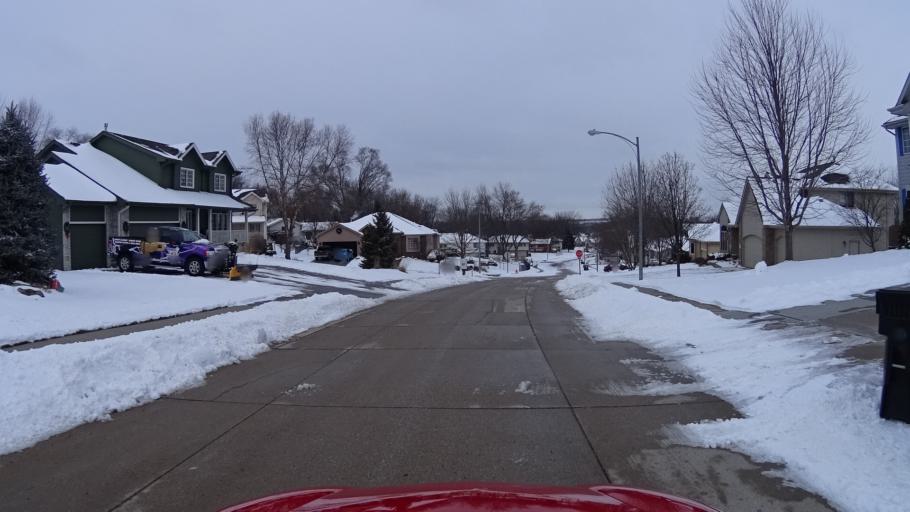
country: US
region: Nebraska
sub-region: Sarpy County
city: Offutt Air Force Base
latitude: 41.1100
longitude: -95.9419
